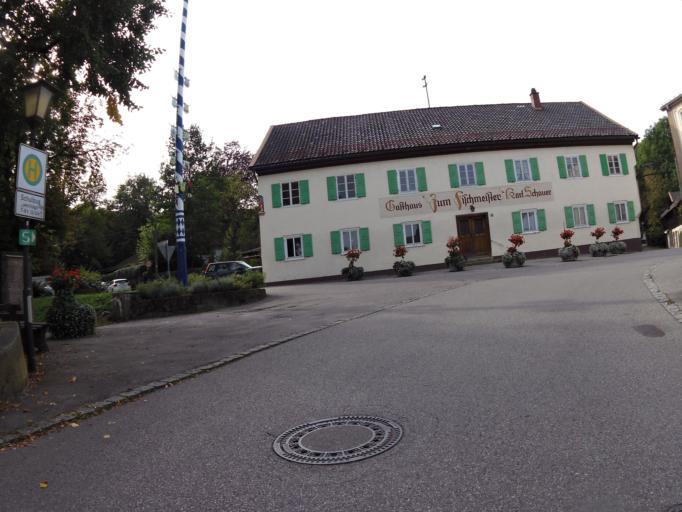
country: DE
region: Bavaria
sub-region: Upper Bavaria
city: Pocking
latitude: 47.9590
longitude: 11.3109
